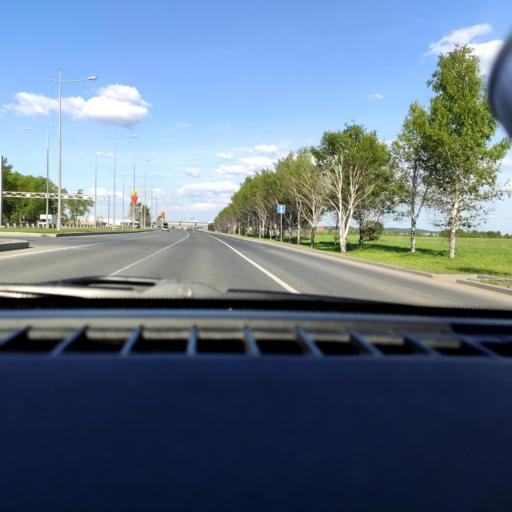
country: RU
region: Perm
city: Kondratovo
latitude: 57.9473
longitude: 56.0903
